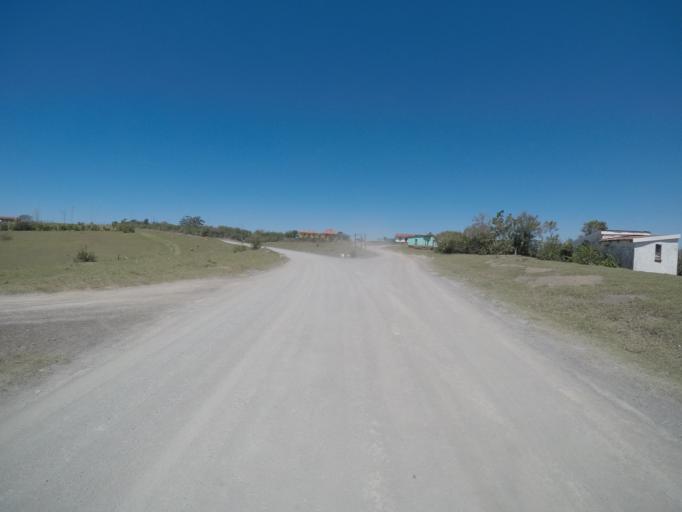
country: ZA
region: Eastern Cape
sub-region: OR Tambo District Municipality
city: Libode
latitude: -32.0014
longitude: 29.0699
